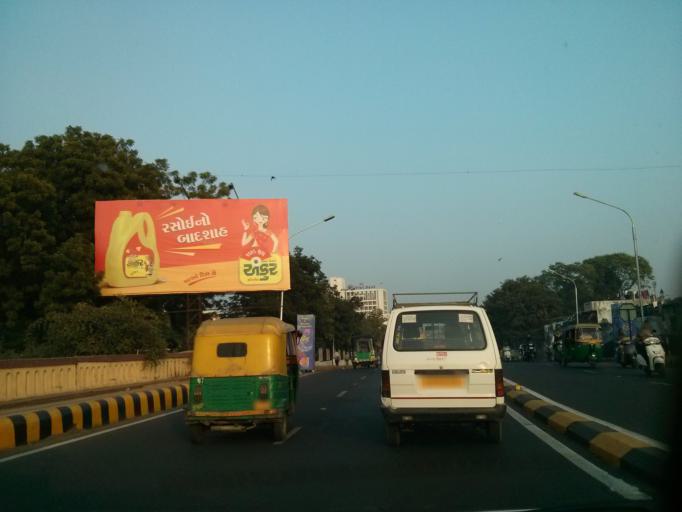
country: IN
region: Gujarat
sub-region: Ahmadabad
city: Ahmedabad
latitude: 23.0272
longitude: 72.5767
